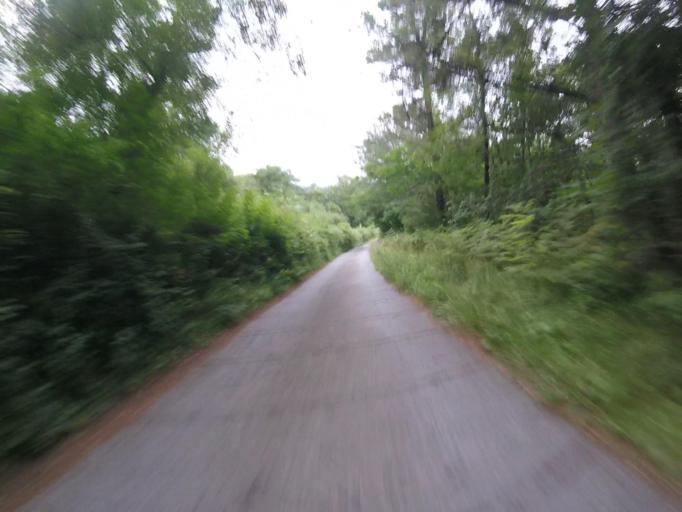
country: ES
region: Basque Country
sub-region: Provincia de Guipuzcoa
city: Lezo
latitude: 43.3107
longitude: -1.8679
